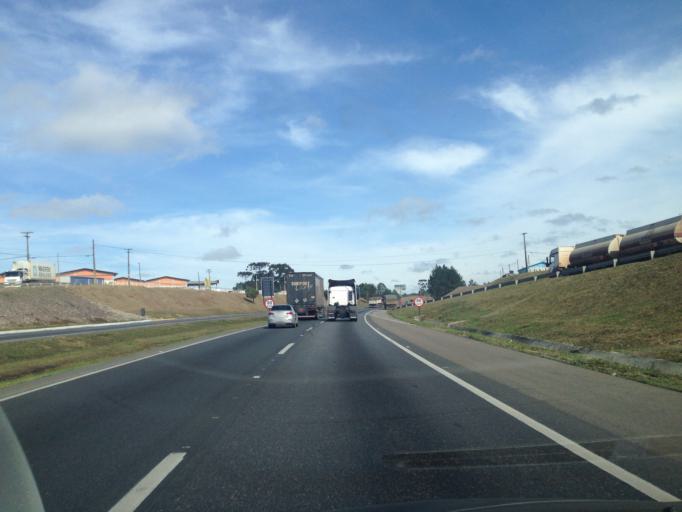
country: BR
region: Parana
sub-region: Sao Jose Dos Pinhais
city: Sao Jose dos Pinhais
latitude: -25.5607
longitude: -49.1518
